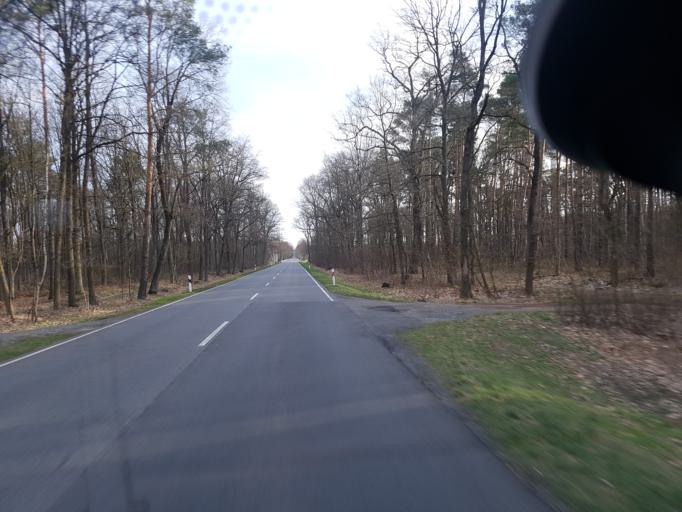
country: DE
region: Brandenburg
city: Luebben
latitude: 51.9705
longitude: 13.9521
